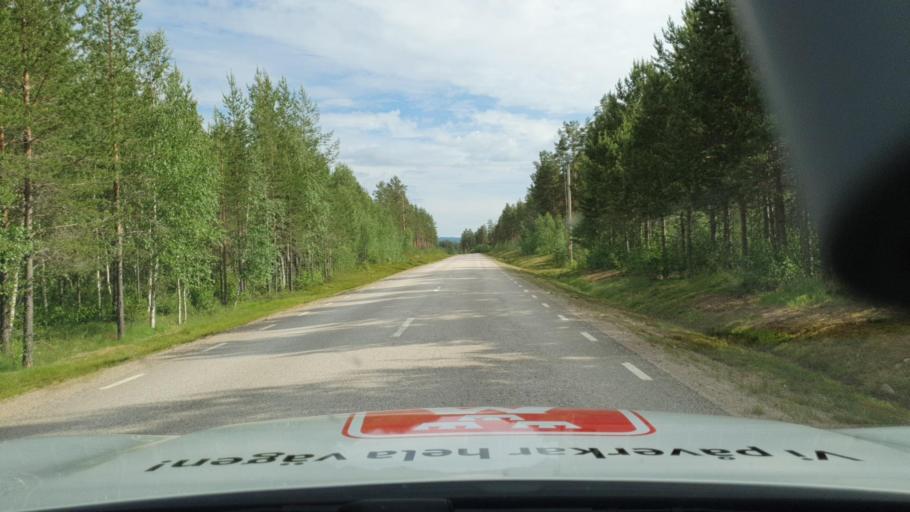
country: NO
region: Hedmark
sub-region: Trysil
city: Innbygda
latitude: 60.9505
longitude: 12.4685
